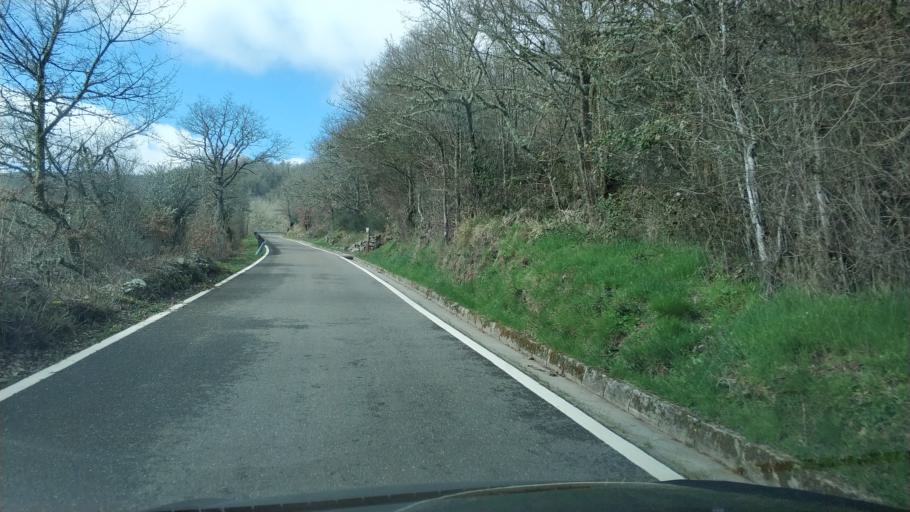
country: ES
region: Castille and Leon
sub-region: Provincia de Palencia
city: Berzosilla
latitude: 42.9000
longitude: -4.0375
